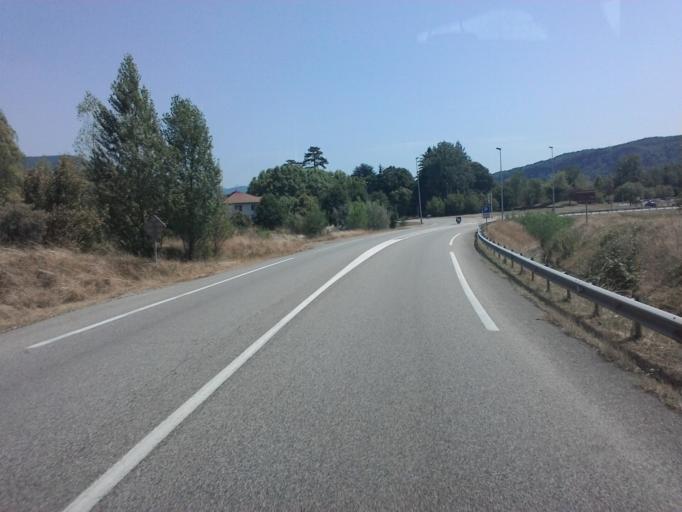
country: FR
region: Rhone-Alpes
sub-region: Departement de l'Ain
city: Lagnieu
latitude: 45.8862
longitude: 5.3458
